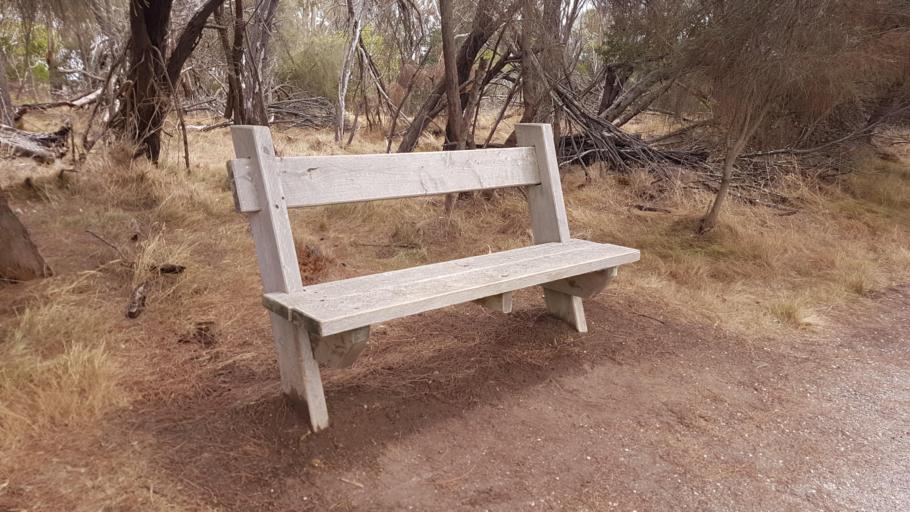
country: AU
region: Victoria
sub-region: Bass Coast
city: Cowes
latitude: -38.4583
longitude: 145.2912
